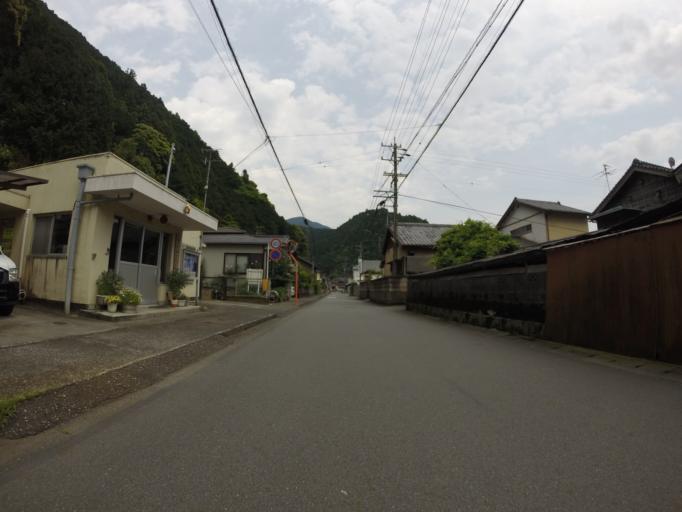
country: JP
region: Shizuoka
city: Shizuoka-shi
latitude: 35.1093
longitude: 138.3643
